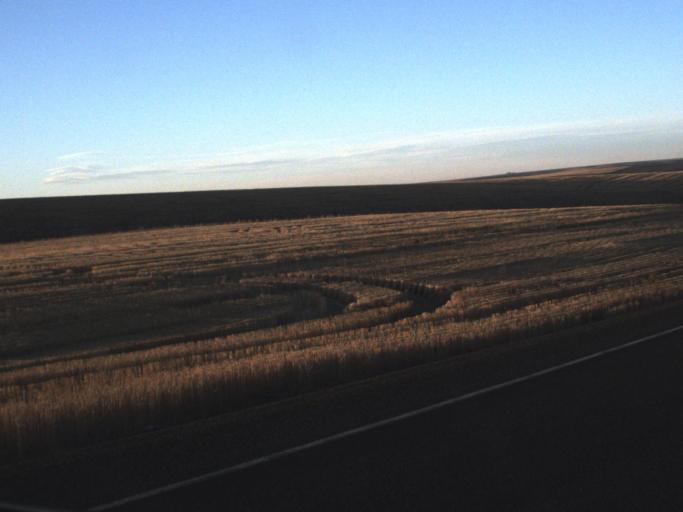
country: US
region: Washington
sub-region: Adams County
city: Ritzville
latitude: 46.9511
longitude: -118.5644
